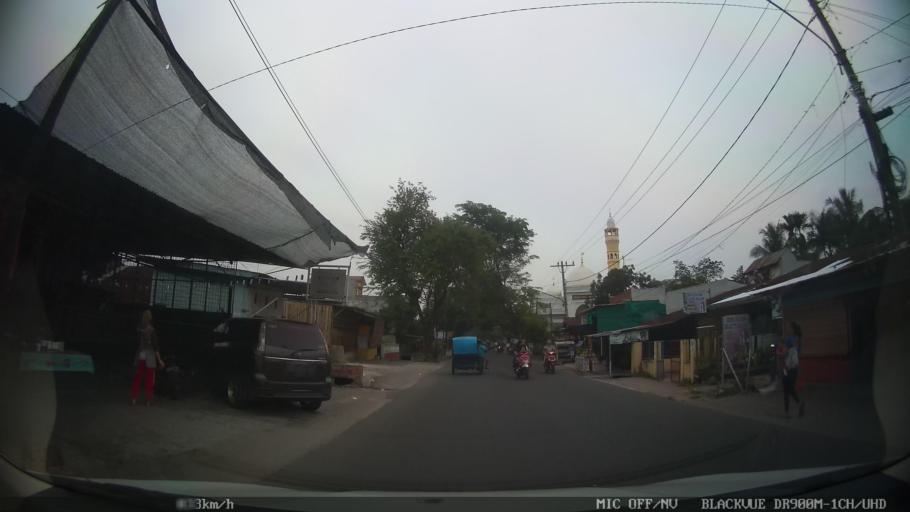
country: ID
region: North Sumatra
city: Deli Tua
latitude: 3.5525
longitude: 98.7087
